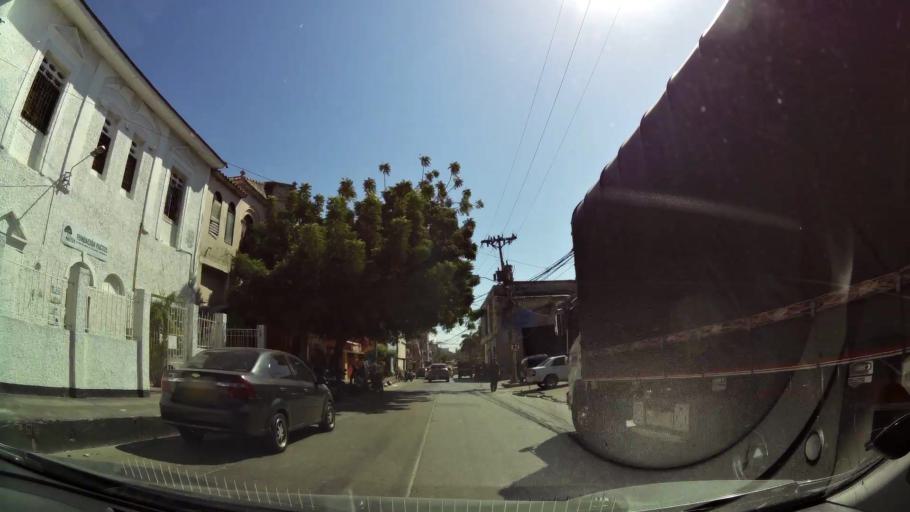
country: CO
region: Atlantico
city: Barranquilla
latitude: 10.9818
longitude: -74.7855
